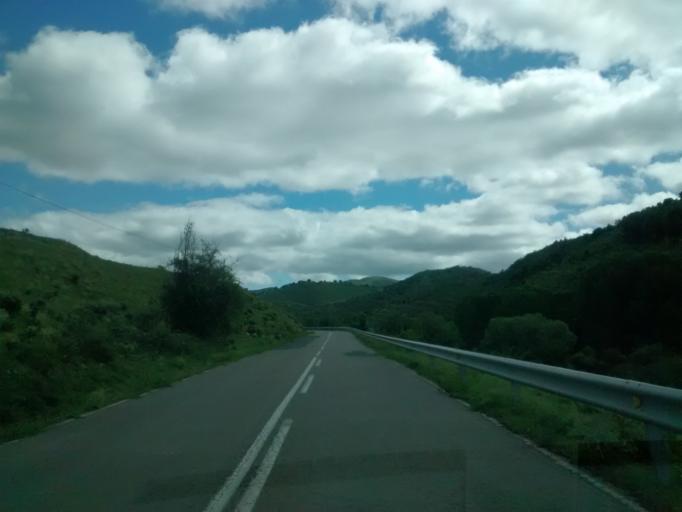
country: ES
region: La Rioja
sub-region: Provincia de La Rioja
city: San Roman de Cameros
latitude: 42.2429
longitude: -2.4614
